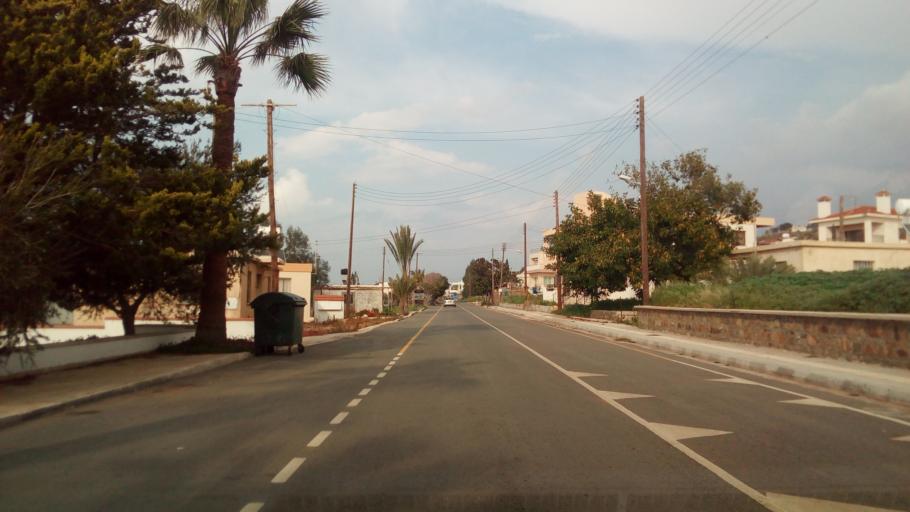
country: CY
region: Lefkosia
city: Kato Pyrgos
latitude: 35.1664
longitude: 32.5476
